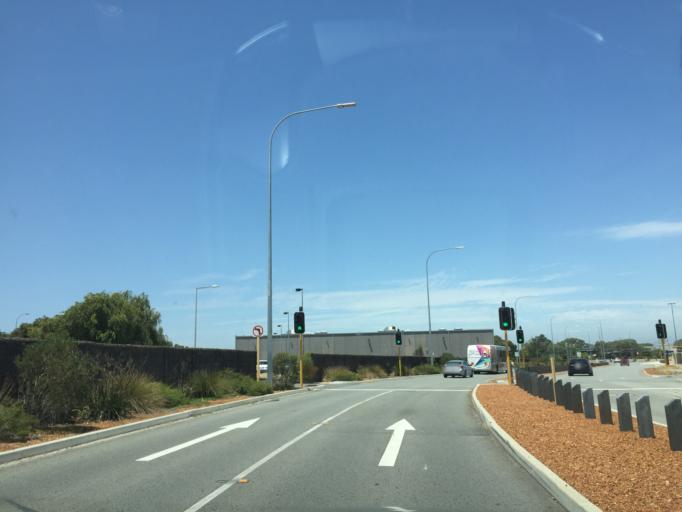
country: AU
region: Western Australia
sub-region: Belmont
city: Redcliffe
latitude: -31.9439
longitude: 115.9766
